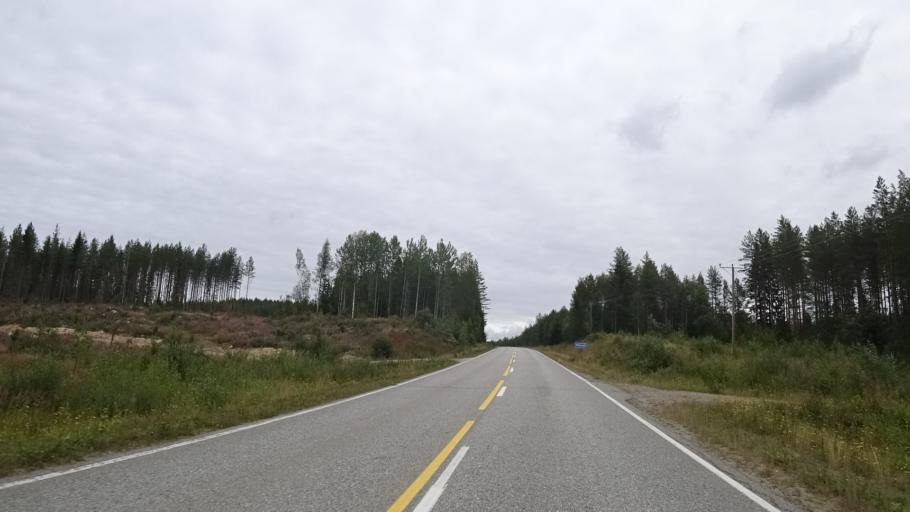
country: FI
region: North Karelia
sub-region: Joensuu
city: Ilomantsi
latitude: 62.6295
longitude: 31.2719
